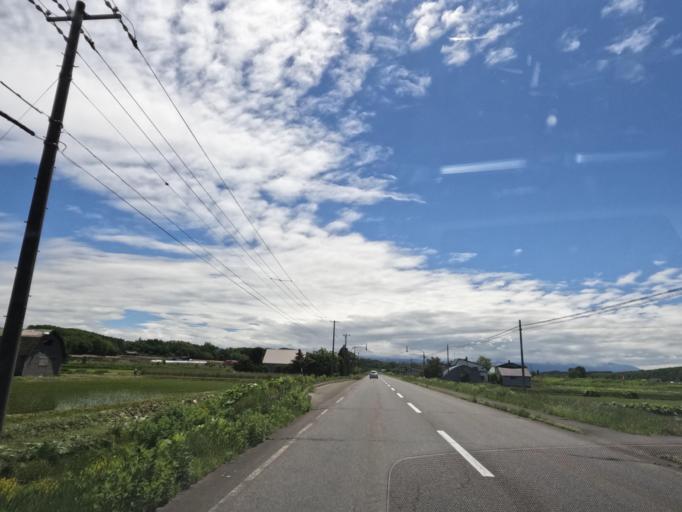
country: JP
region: Hokkaido
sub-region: Asahikawa-shi
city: Asahikawa
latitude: 43.6561
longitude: 142.4386
